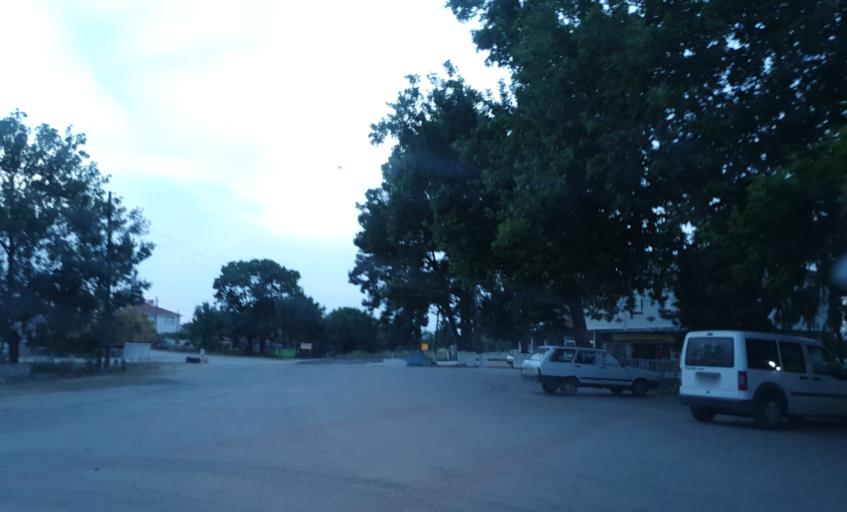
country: TR
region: Kirklareli
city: Vize
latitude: 41.4879
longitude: 27.7532
